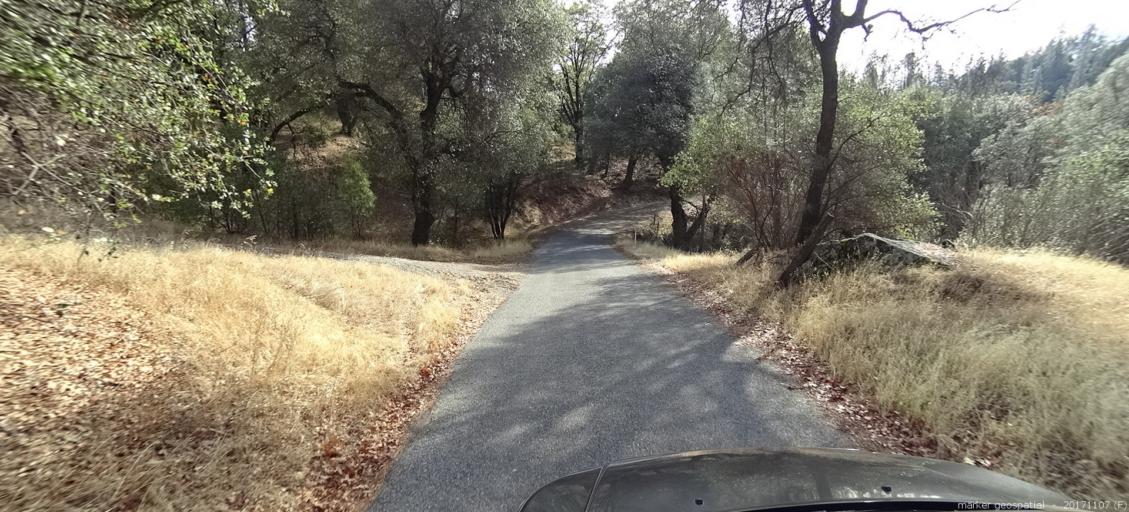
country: US
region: California
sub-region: Shasta County
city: Shasta
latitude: 40.5404
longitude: -122.5673
